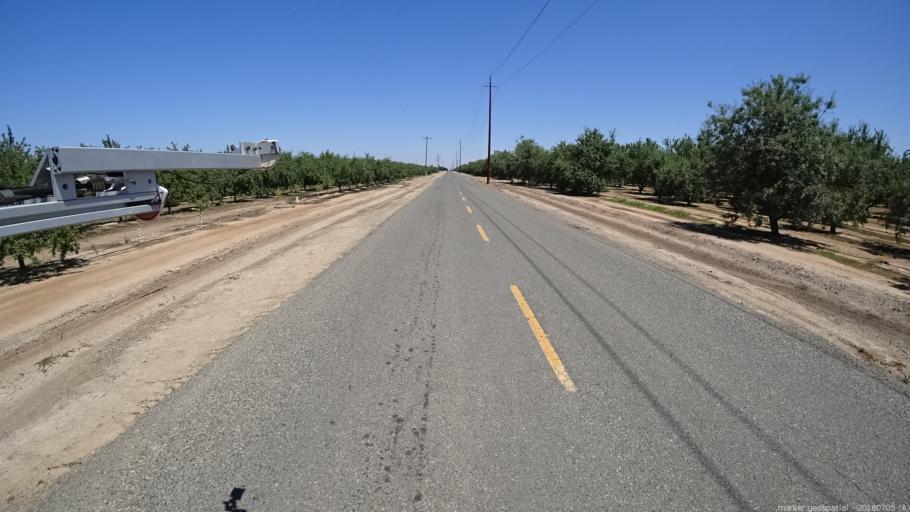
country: US
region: California
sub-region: Madera County
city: Chowchilla
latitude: 37.1533
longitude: -120.2021
